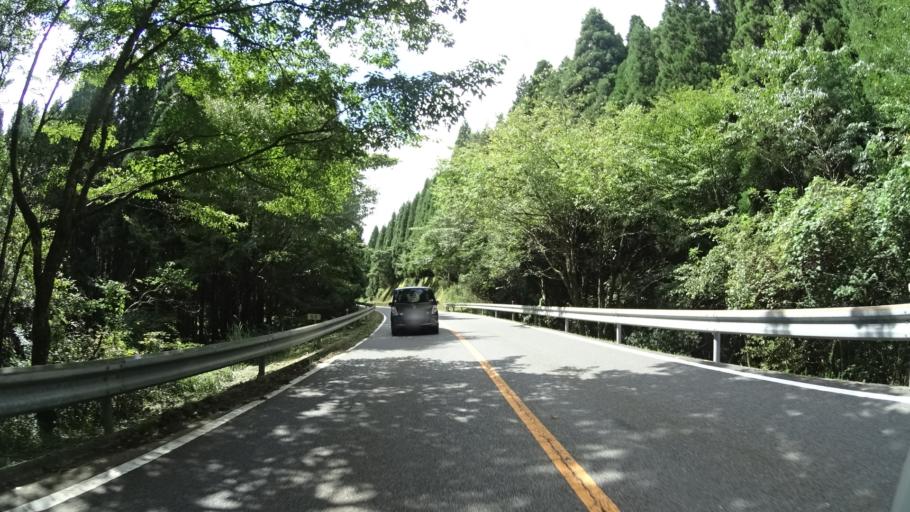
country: JP
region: Oita
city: Tsukawaki
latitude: 33.2196
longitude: 131.2984
